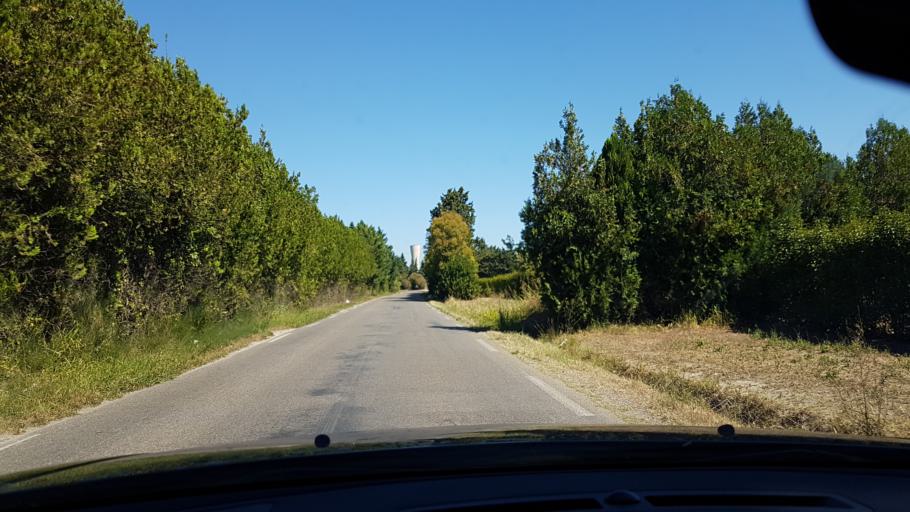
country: FR
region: Provence-Alpes-Cote d'Azur
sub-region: Departement des Bouches-du-Rhone
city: Molleges
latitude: 43.8155
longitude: 4.9481
